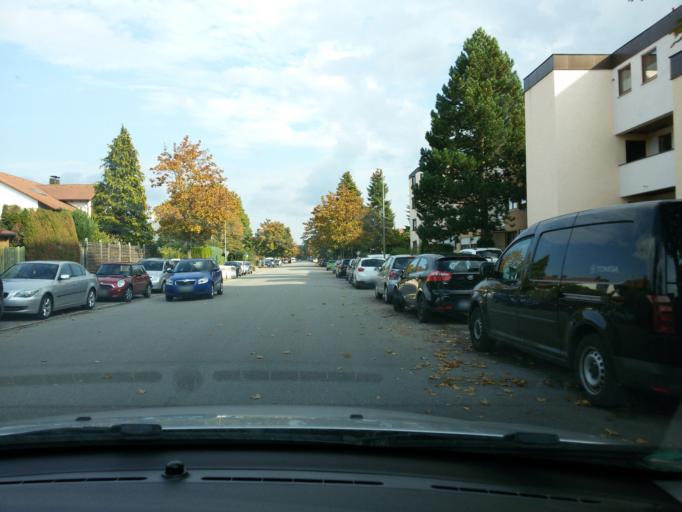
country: DE
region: Bavaria
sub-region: Swabia
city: Buchloe
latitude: 48.0304
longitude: 10.7200
